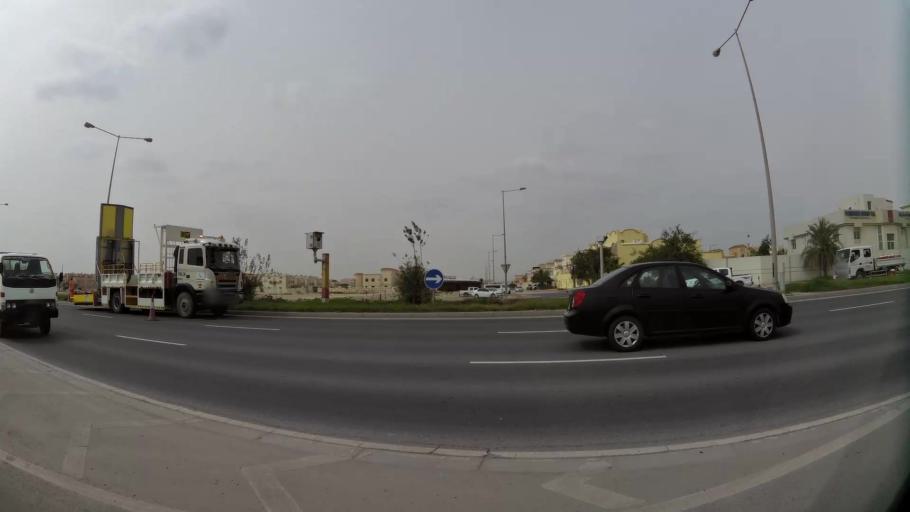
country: QA
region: Baladiyat ad Dawhah
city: Doha
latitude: 25.2376
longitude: 51.5343
